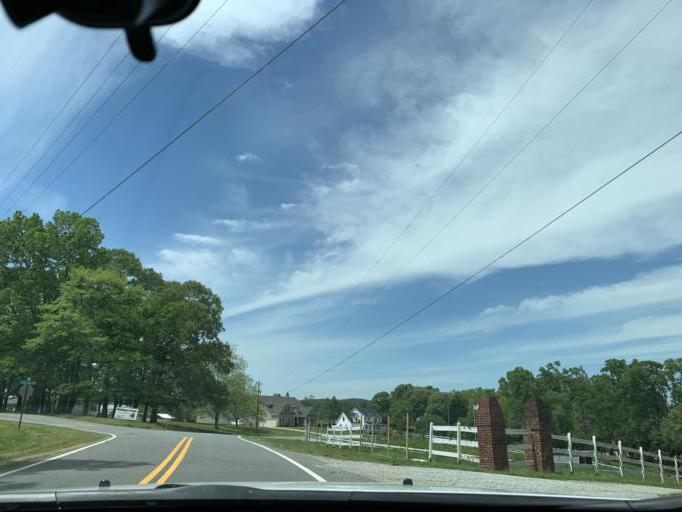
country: US
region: Georgia
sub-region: Hall County
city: Flowery Branch
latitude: 34.2683
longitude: -84.0233
